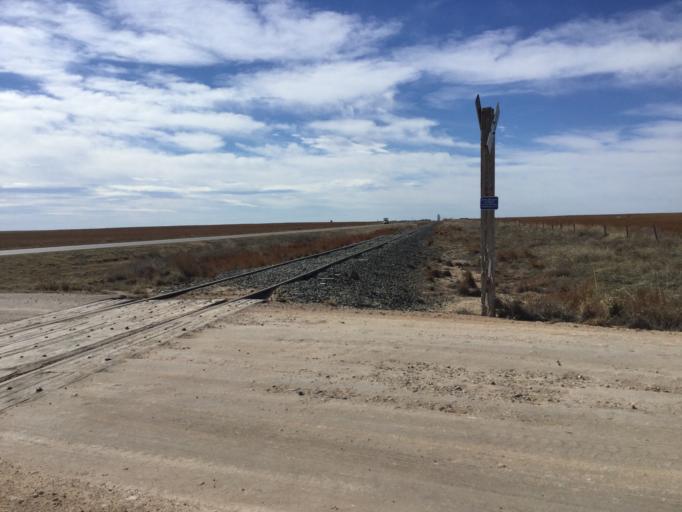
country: US
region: Kansas
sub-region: Stevens County
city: Hugoton
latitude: 37.1344
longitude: -101.5738
